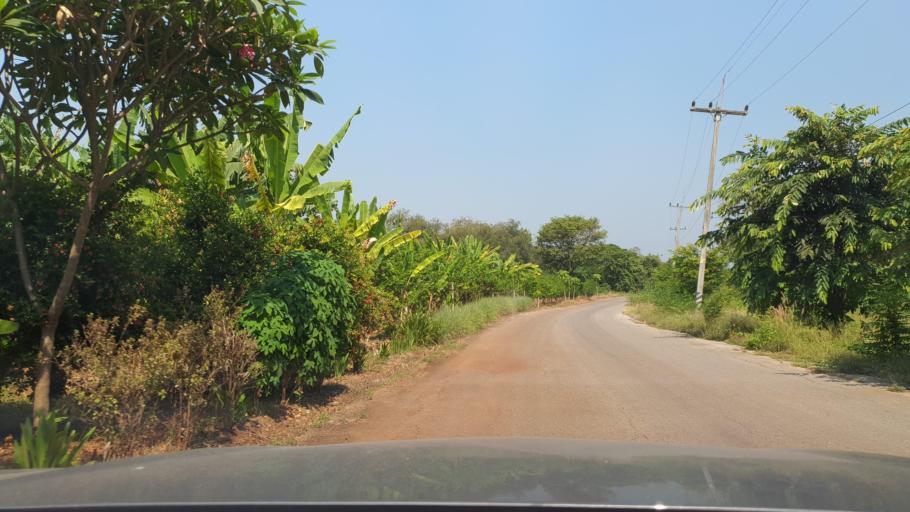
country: TH
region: Kanchanaburi
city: Sai Yok
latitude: 14.0984
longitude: 99.1719
